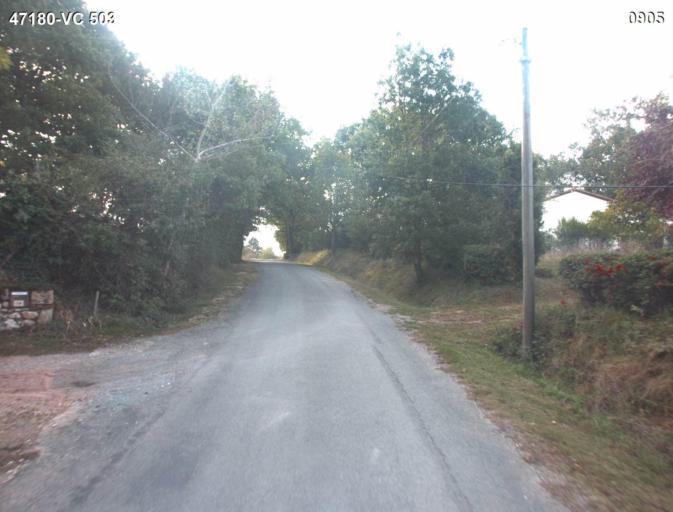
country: FR
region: Aquitaine
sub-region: Departement du Lot-et-Garonne
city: Sainte-Colombe-en-Bruilhois
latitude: 44.1757
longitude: 0.4323
